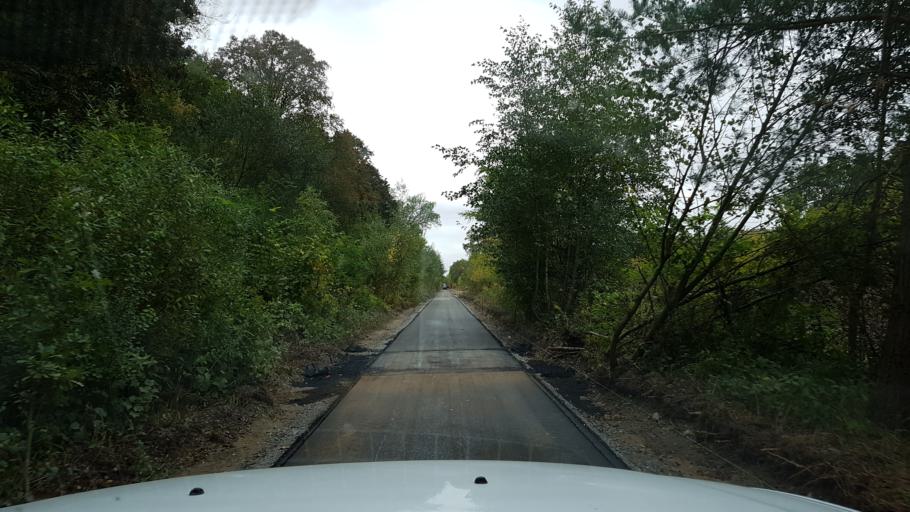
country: PL
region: West Pomeranian Voivodeship
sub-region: Powiat gryfinski
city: Cedynia
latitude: 52.8231
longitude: 14.2372
